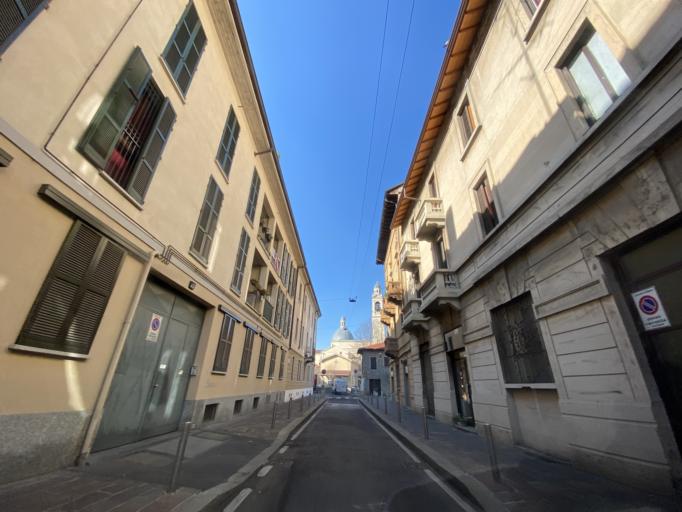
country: IT
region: Lombardy
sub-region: Citta metropolitana di Milano
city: Novate Milanese
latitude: 45.5006
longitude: 9.1494
